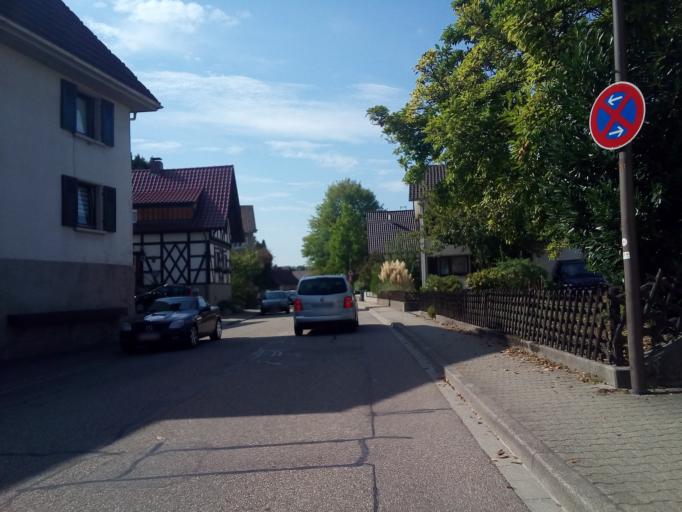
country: DE
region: Baden-Wuerttemberg
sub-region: Karlsruhe Region
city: Ottersweier
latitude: 48.6676
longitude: 8.1136
